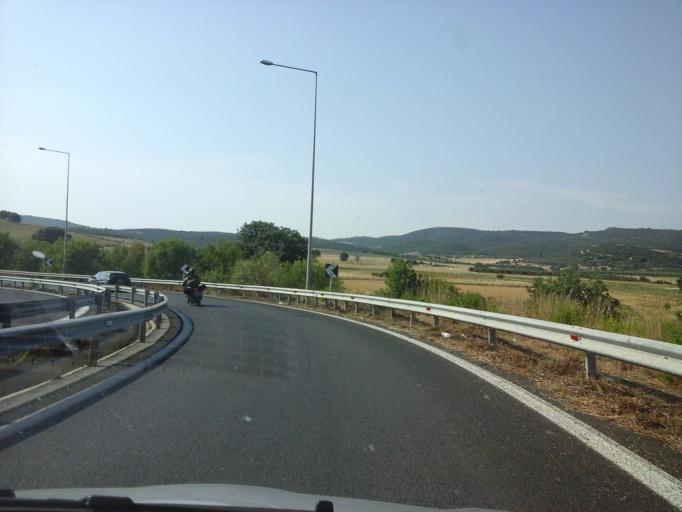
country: GR
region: East Macedonia and Thrace
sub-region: Nomos Evrou
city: Alexandroupoli
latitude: 40.8789
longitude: 25.8593
